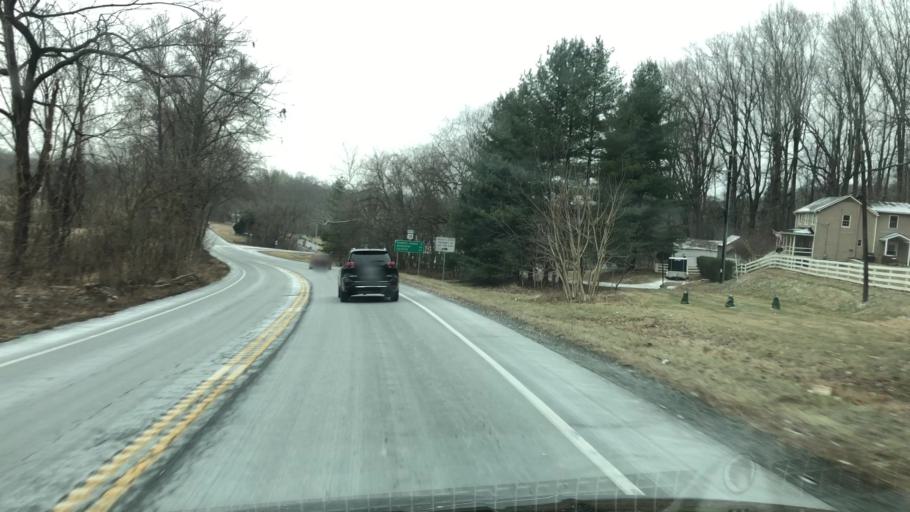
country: US
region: Virginia
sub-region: Loudoun County
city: Brambleton
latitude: 39.0347
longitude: -77.6250
